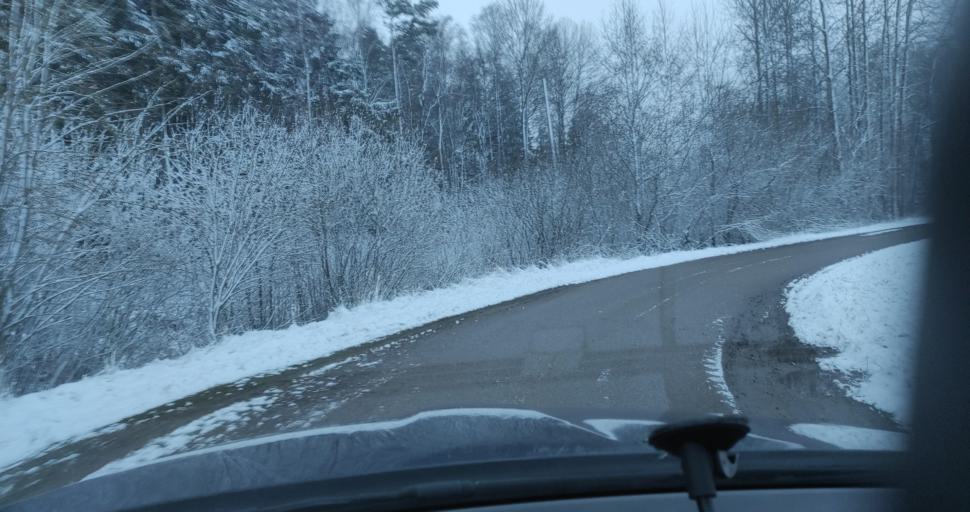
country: LV
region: Skrunda
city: Skrunda
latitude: 56.8670
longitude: 22.2391
